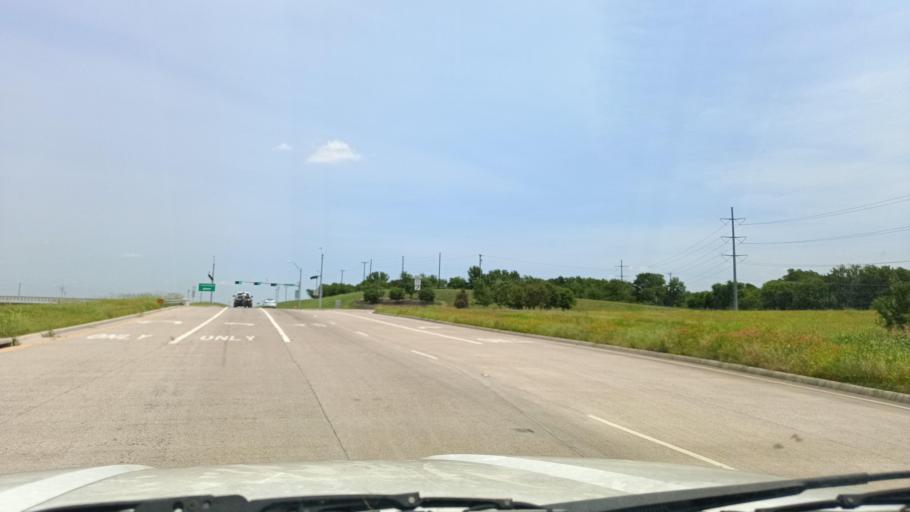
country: US
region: Texas
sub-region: Bell County
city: Temple
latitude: 31.1176
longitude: -97.3850
